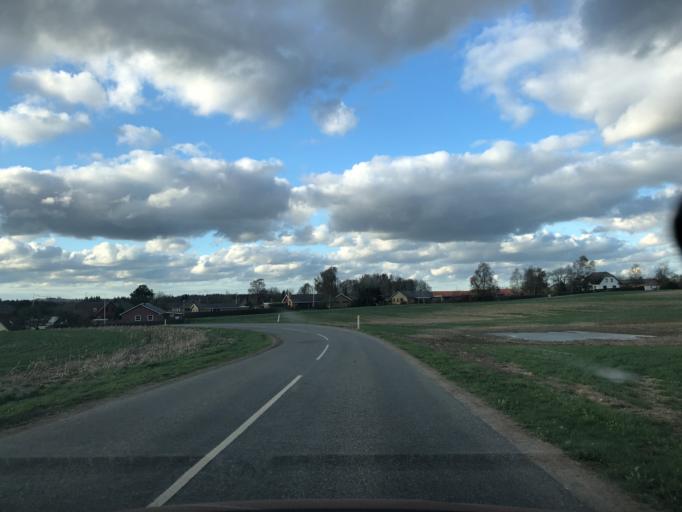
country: DK
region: Zealand
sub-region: Lejre Kommune
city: Kirke Hvalso
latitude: 55.5150
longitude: 11.8736
